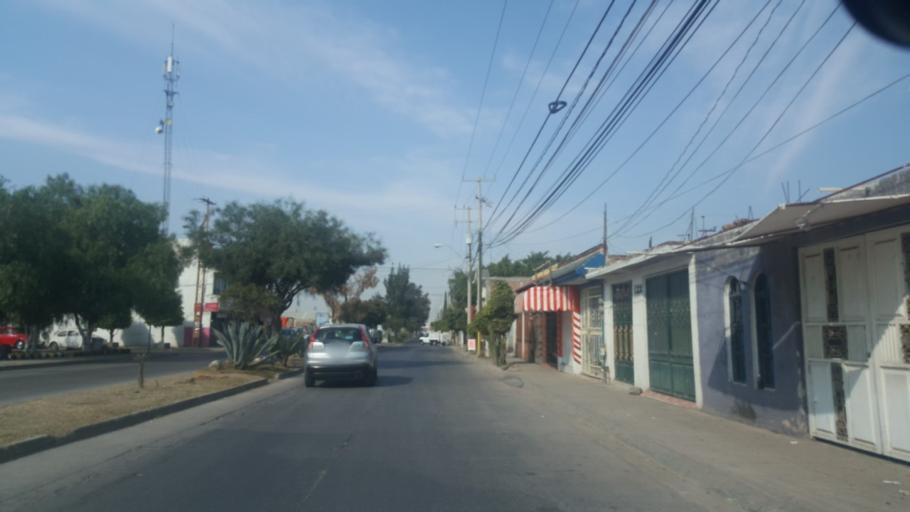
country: MX
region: Guanajuato
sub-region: Leon
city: Fraccionamiento Paraiso Real
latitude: 21.1032
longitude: -101.6163
